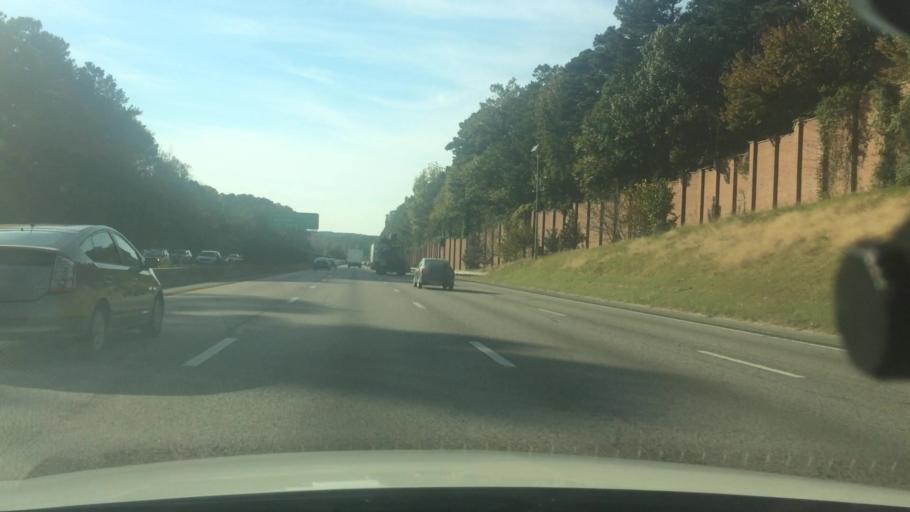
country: US
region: North Carolina
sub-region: Wake County
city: West Raleigh
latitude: 35.8362
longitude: -78.6521
